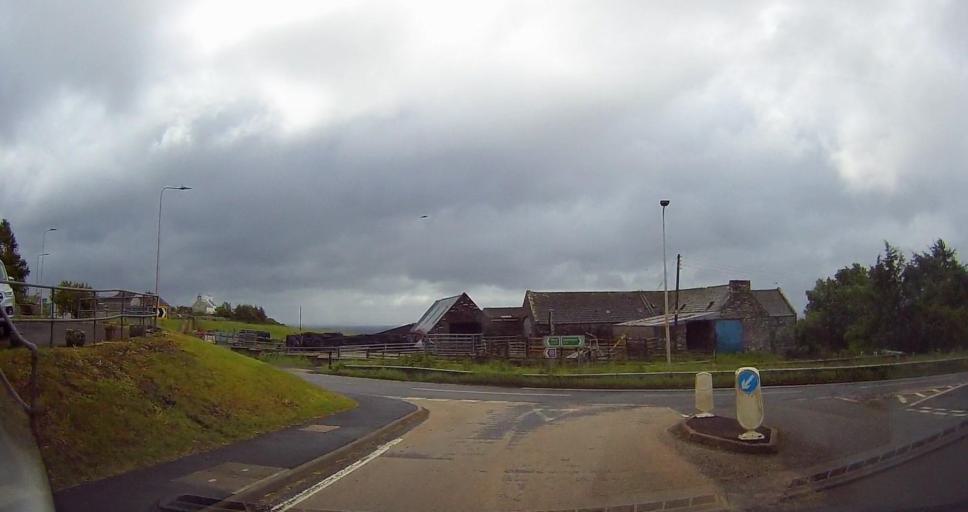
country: GB
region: Scotland
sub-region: Highland
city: Wick
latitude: 58.2834
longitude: -3.3671
